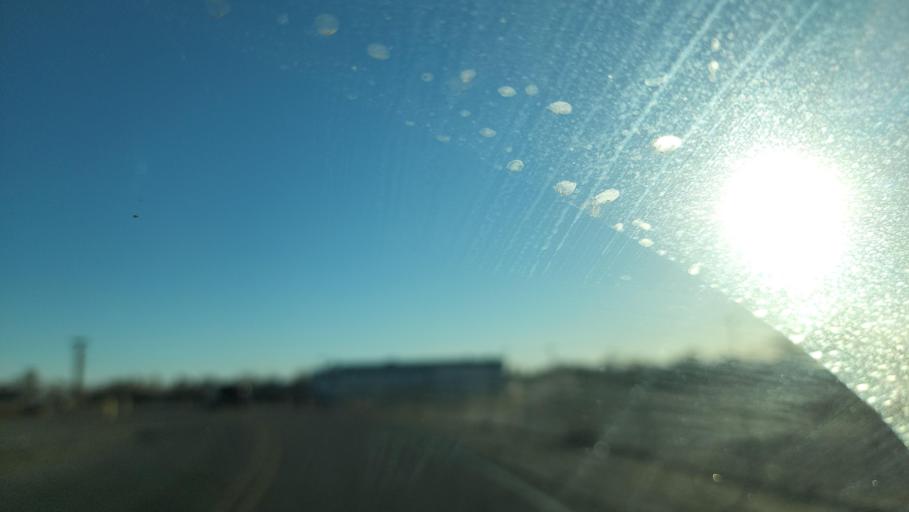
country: US
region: New Mexico
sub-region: Bernalillo County
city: South Valley
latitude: 35.0247
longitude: -106.6541
